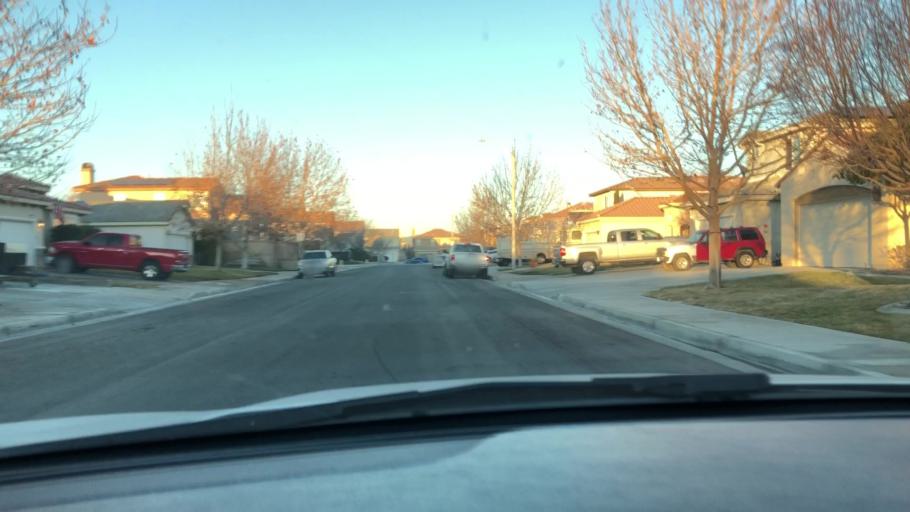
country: US
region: California
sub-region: Los Angeles County
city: Quartz Hill
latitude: 34.6807
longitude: -118.2047
